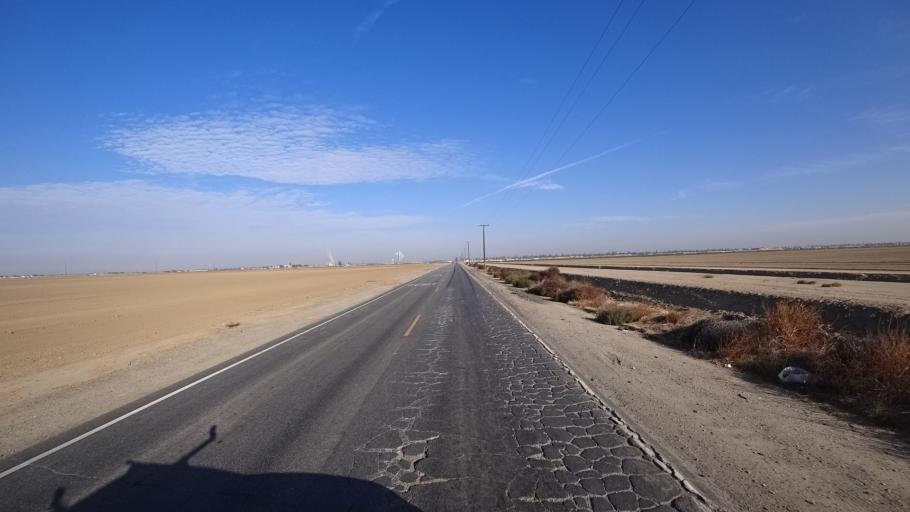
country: US
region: California
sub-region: Kern County
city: Greenfield
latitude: 35.2827
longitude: -119.0922
